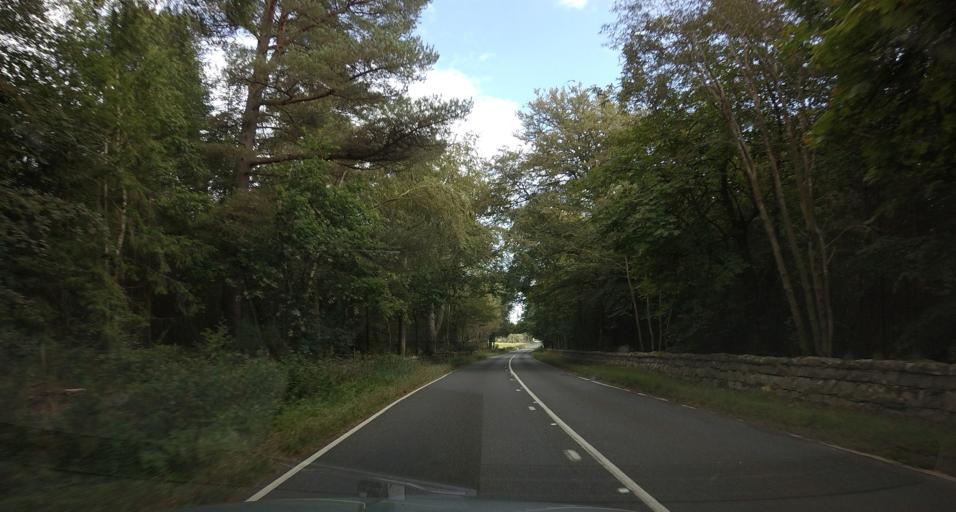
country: GB
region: Scotland
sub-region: Aberdeenshire
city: Kintore
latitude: 57.1649
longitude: -2.3639
